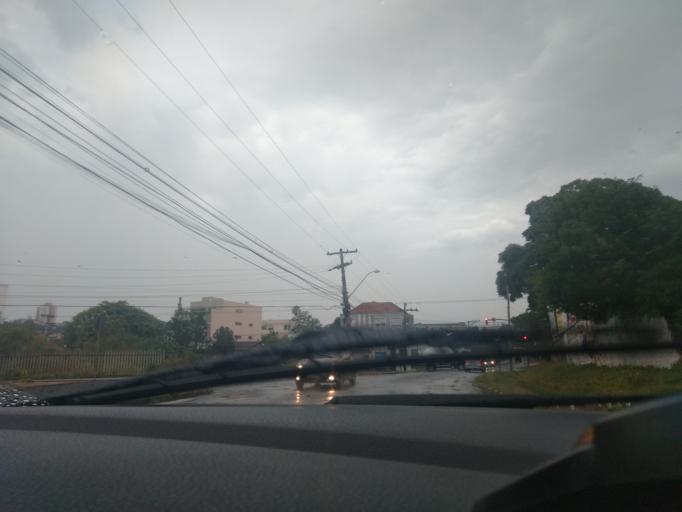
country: BR
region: Rio Grande do Sul
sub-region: Porto Alegre
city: Porto Alegre
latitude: -30.0689
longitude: -51.2086
